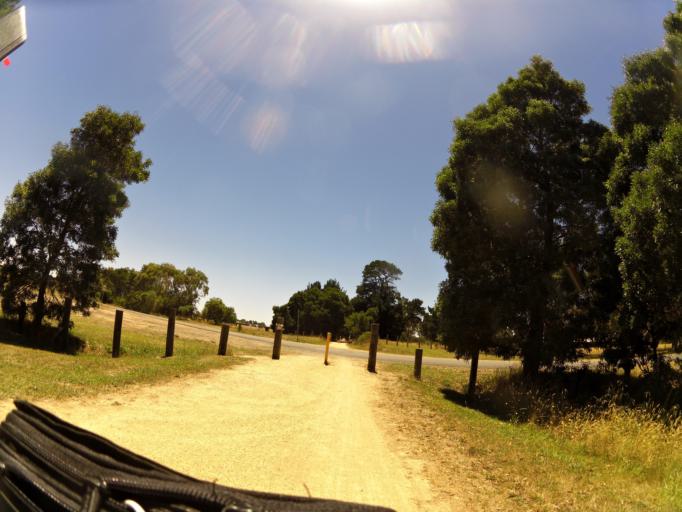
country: AU
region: Victoria
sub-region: Ballarat North
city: Delacombe
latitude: -37.5785
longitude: 143.7269
